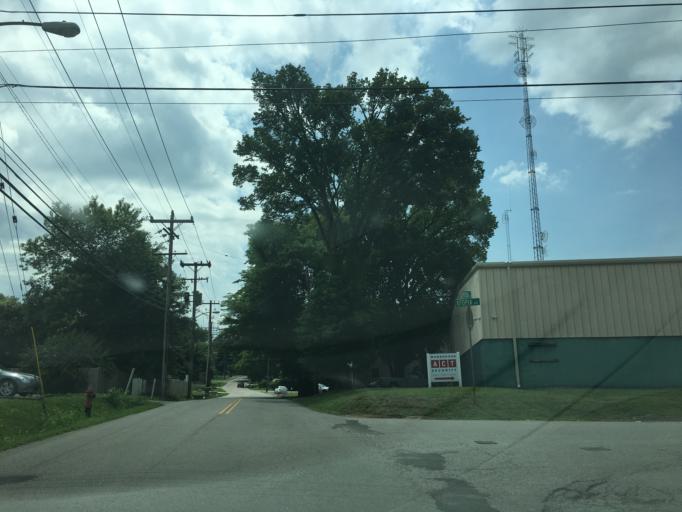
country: US
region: Tennessee
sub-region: Davidson County
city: Oak Hill
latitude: 36.1248
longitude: -86.7563
